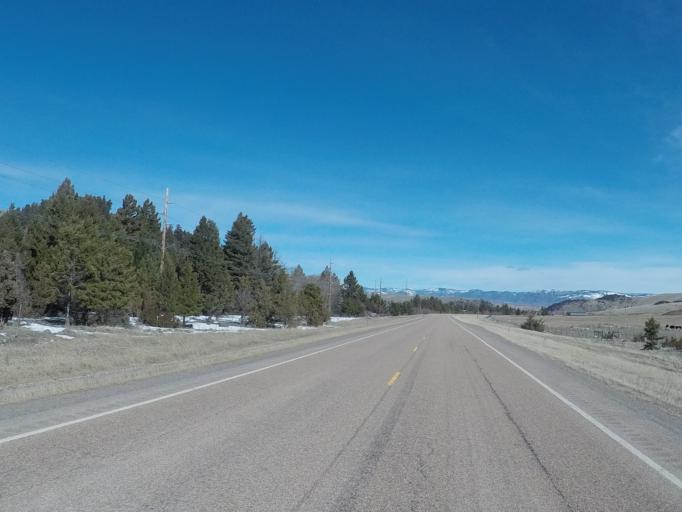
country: US
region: Montana
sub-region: Granite County
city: Philipsburg
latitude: 46.4768
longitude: -113.2346
